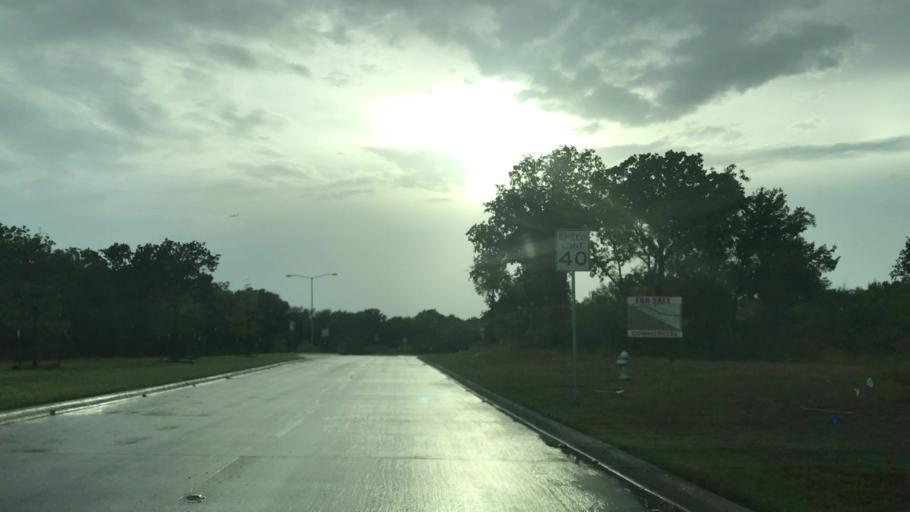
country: US
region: Texas
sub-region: Denton County
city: Lewisville
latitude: 33.0569
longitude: -96.9933
